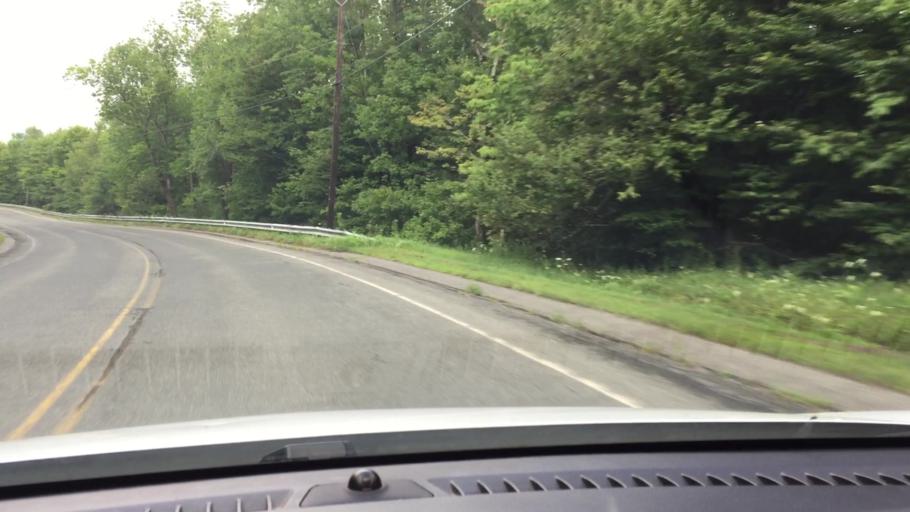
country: US
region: Massachusetts
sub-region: Berkshire County
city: Hinsdale
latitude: 42.4454
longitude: -73.0561
